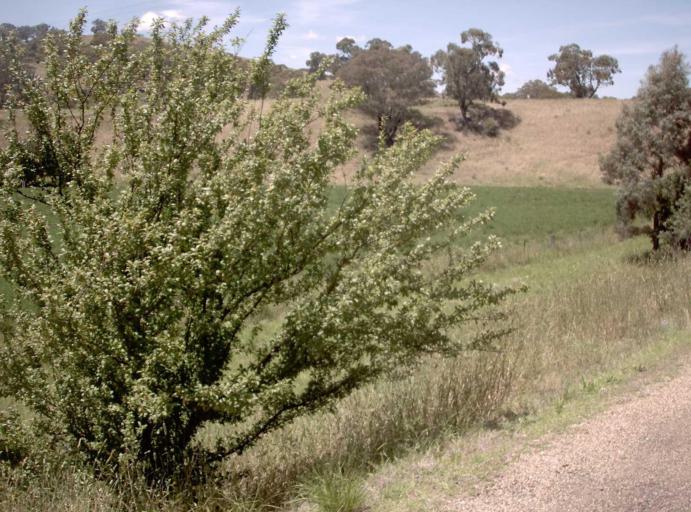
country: AU
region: Victoria
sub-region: East Gippsland
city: Bairnsdale
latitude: -37.3820
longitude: 147.8305
